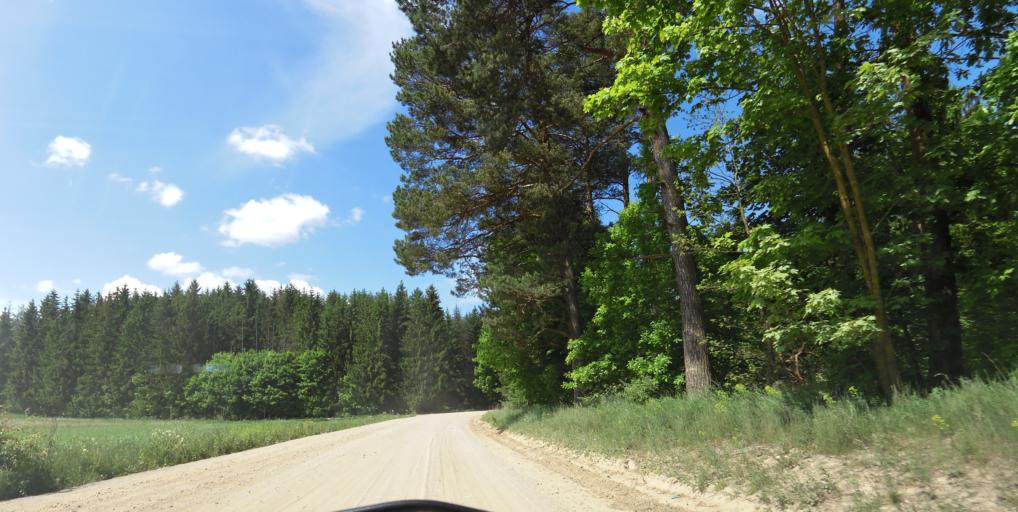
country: LT
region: Vilnius County
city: Pilaite
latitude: 54.7378
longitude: 25.1541
